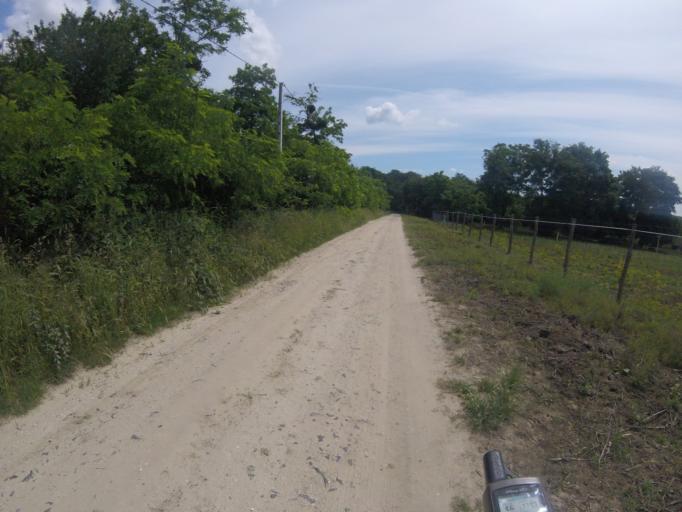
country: HU
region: Zala
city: Zalaszentgrot
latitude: 46.8839
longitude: 17.0351
